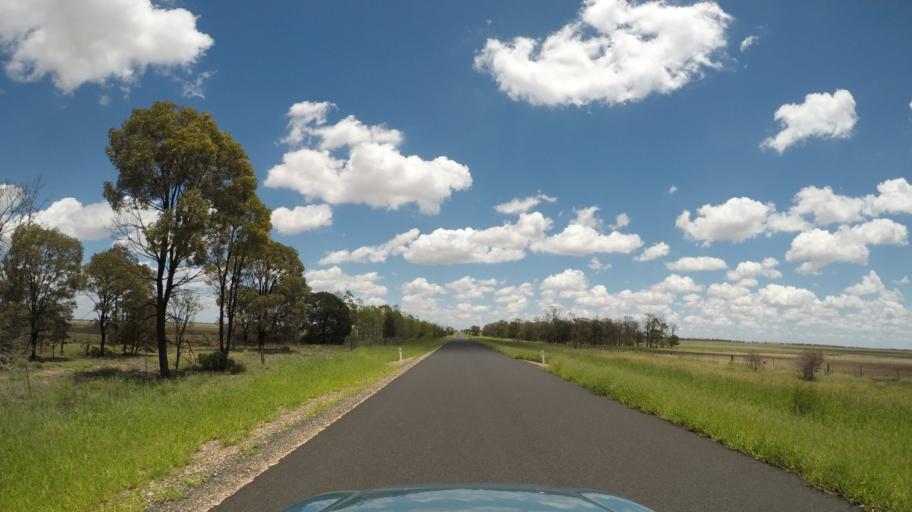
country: AU
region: Queensland
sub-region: Goondiwindi
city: Goondiwindi
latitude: -28.1655
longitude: 150.1733
